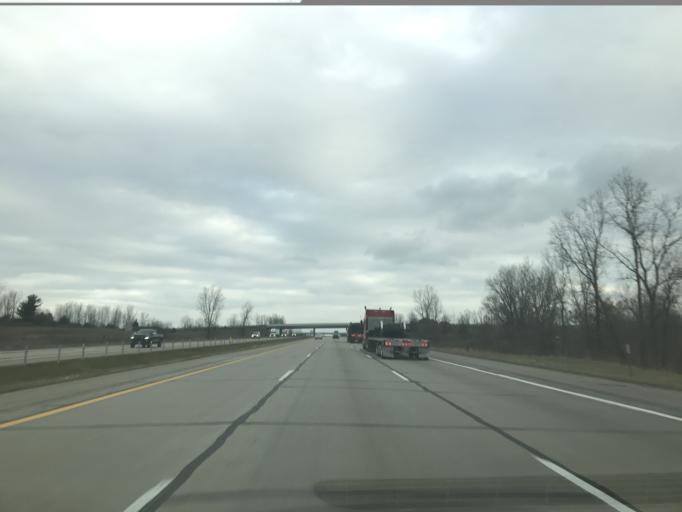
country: US
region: Michigan
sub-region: Eaton County
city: Waverly
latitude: 42.7129
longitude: -84.6692
